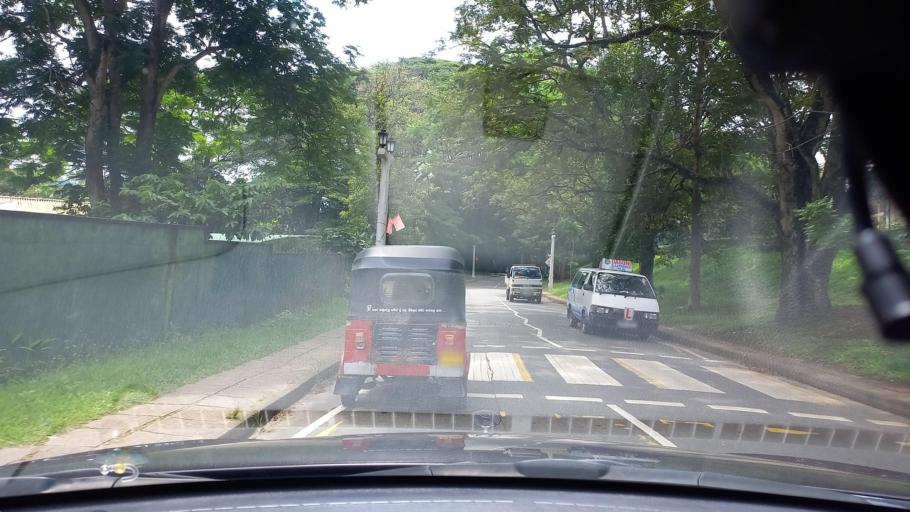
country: LK
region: Central
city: Kandy
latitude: 7.2630
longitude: 80.5983
